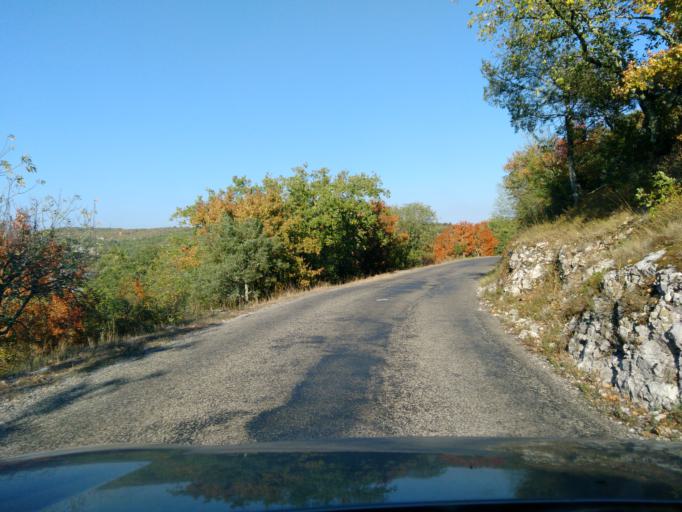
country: FR
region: Rhone-Alpes
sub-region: Departement de l'Ardeche
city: Les Vans
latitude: 44.3936
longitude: 4.1972
